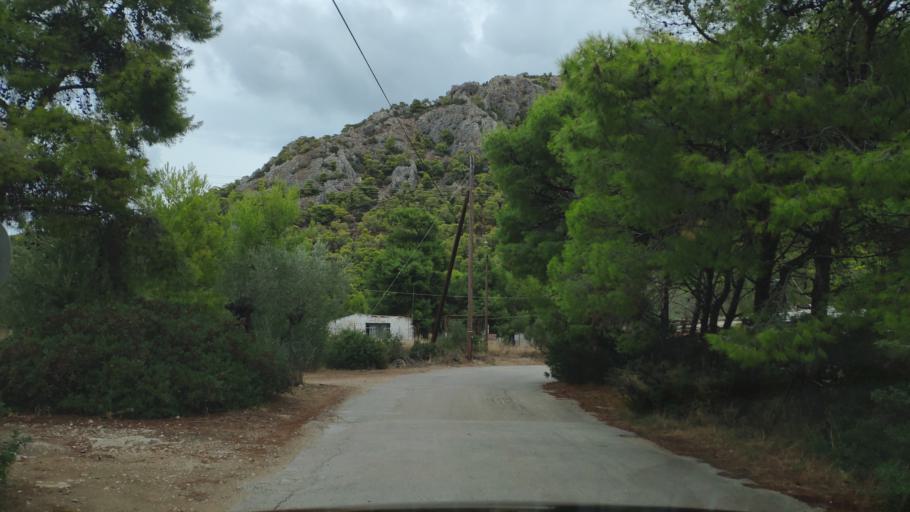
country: GR
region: Peloponnese
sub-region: Nomos Korinthias
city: Perachora
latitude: 38.0319
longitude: 22.8720
